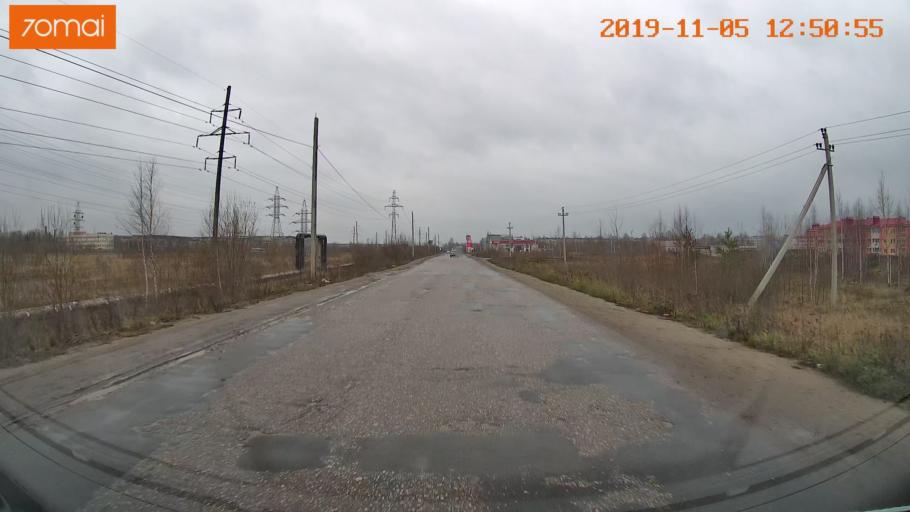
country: RU
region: Ivanovo
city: Kokhma
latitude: 56.9478
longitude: 41.1101
